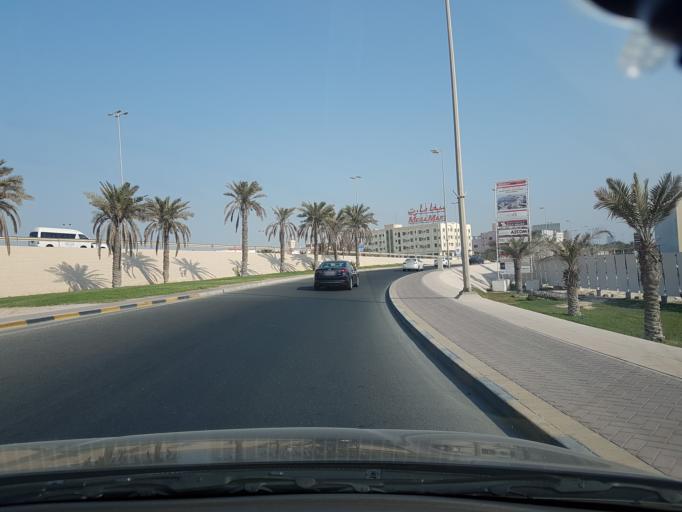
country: BH
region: Muharraq
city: Al Muharraq
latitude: 26.2493
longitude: 50.6056
